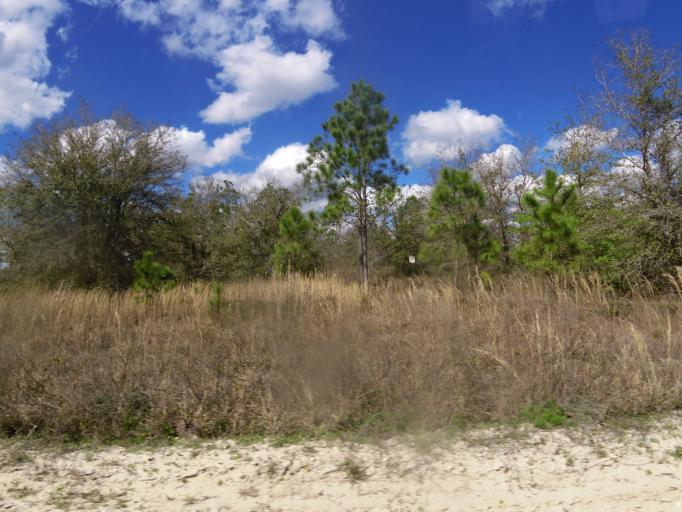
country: US
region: Florida
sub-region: Clay County
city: Green Cove Springs
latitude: 29.8404
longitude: -81.7269
